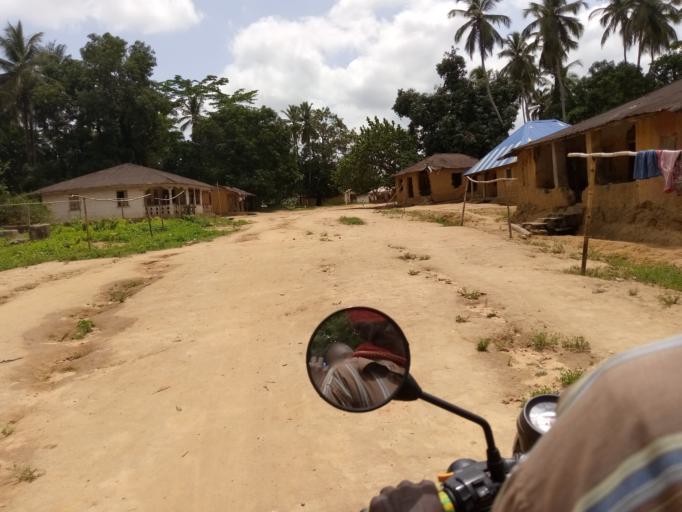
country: SL
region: Western Area
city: Waterloo
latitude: 8.4315
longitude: -13.0125
